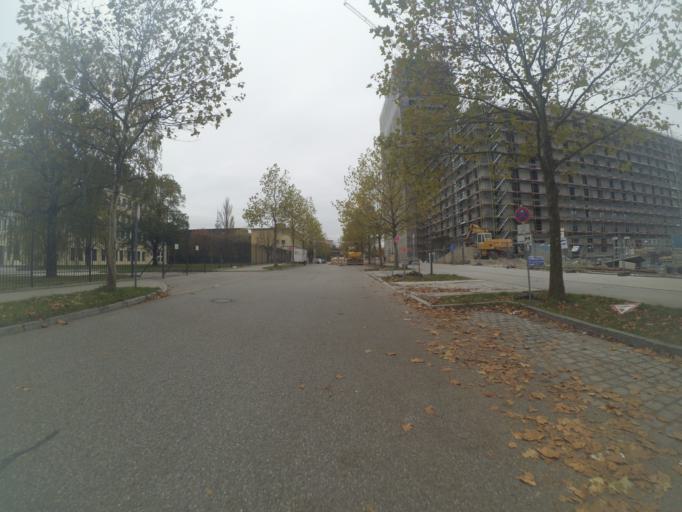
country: DE
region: Bavaria
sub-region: Upper Bavaria
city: Munich
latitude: 48.1877
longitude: 11.5462
